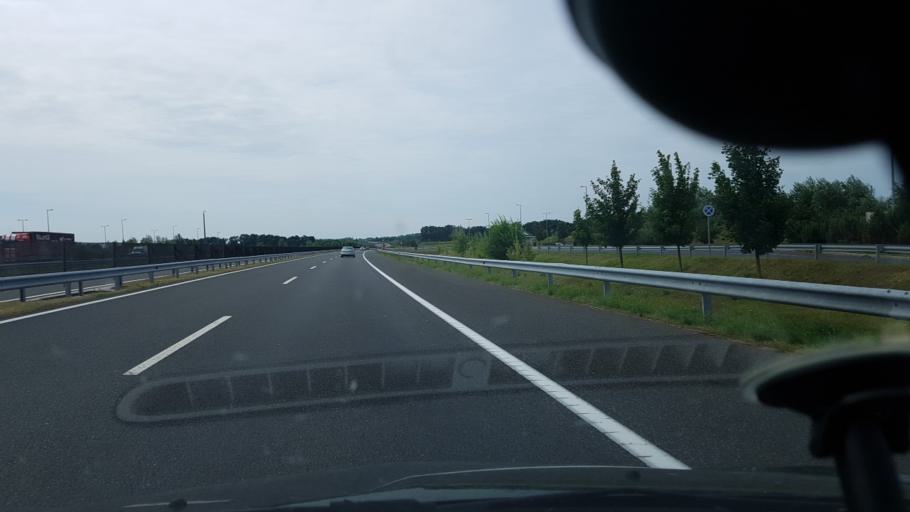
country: HU
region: Somogy
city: Balatonbereny
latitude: 46.6282
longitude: 17.2764
